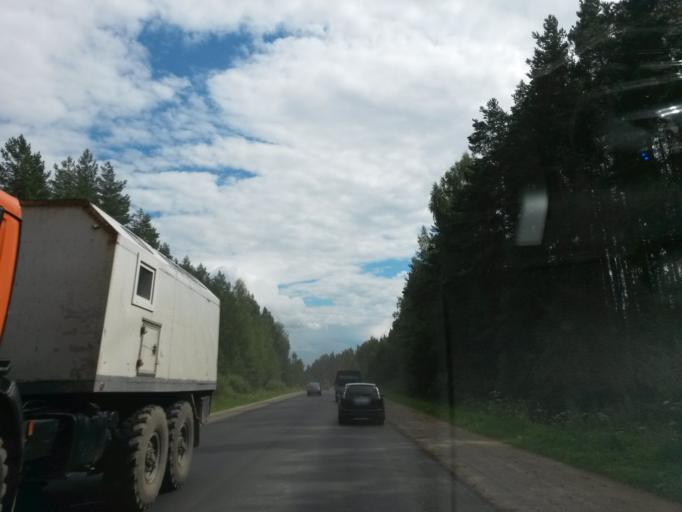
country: RU
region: Ivanovo
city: Novo-Talitsy
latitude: 57.0179
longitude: 40.7810
